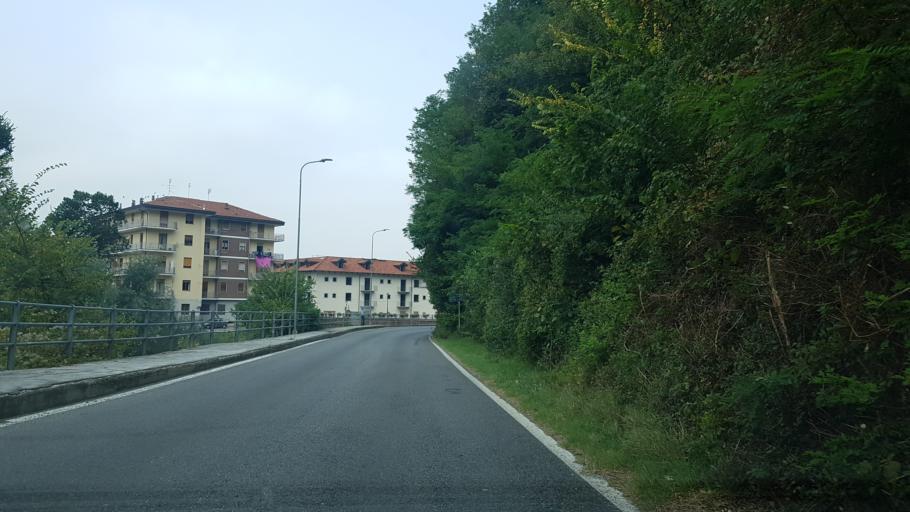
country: IT
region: Piedmont
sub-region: Provincia di Cuneo
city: Chiusa di Pesio
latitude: 44.3243
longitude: 7.6809
